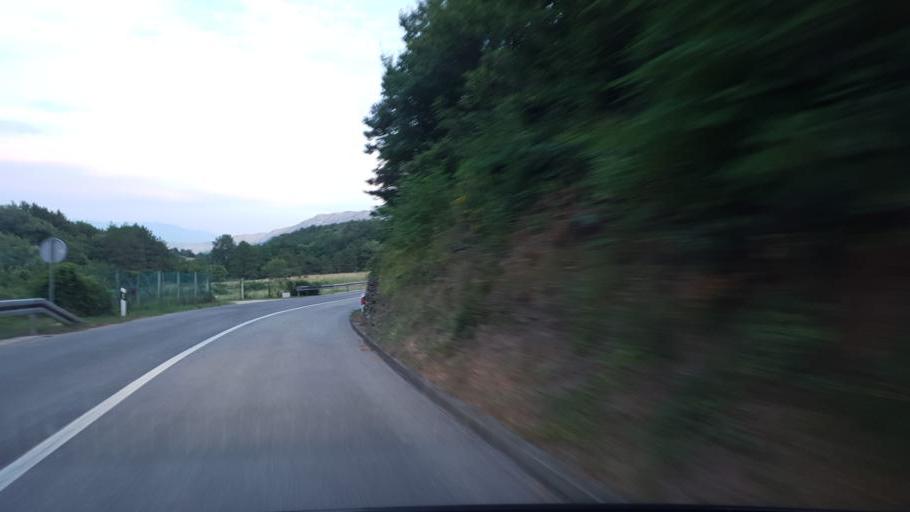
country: HR
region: Primorsko-Goranska
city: Punat
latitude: 45.0080
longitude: 14.7022
